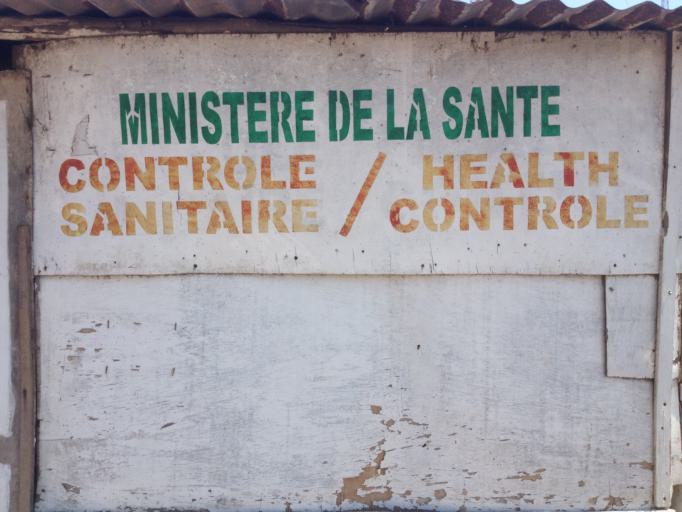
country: TG
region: Maritime
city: Aneho
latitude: 6.2407
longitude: 1.6288
